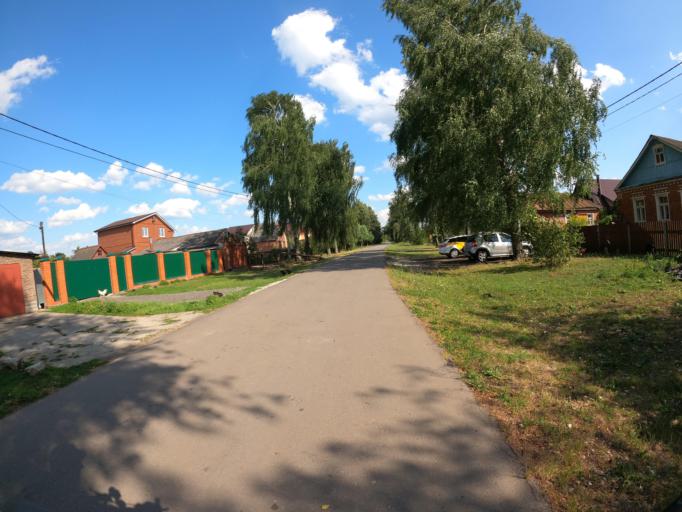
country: RU
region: Moskovskaya
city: Peski
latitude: 55.2120
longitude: 38.7349
